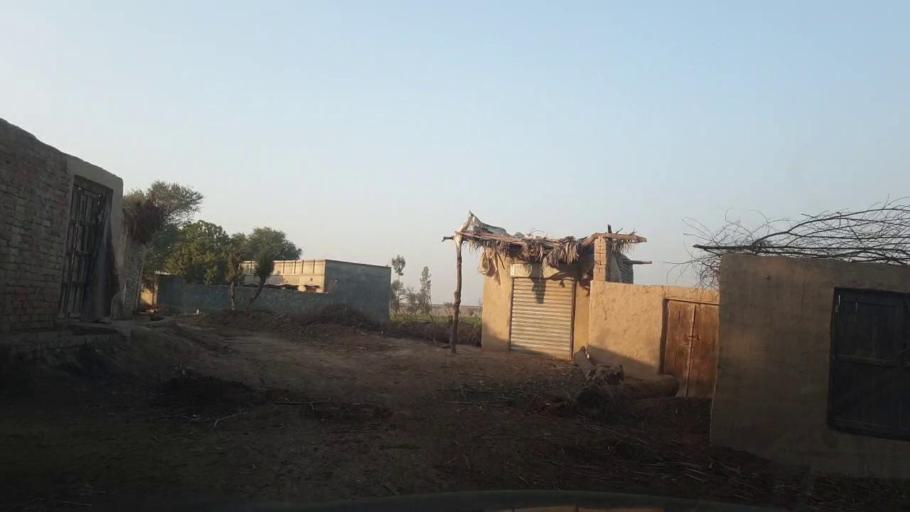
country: PK
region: Sindh
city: Ubauro
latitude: 28.3203
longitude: 69.7759
